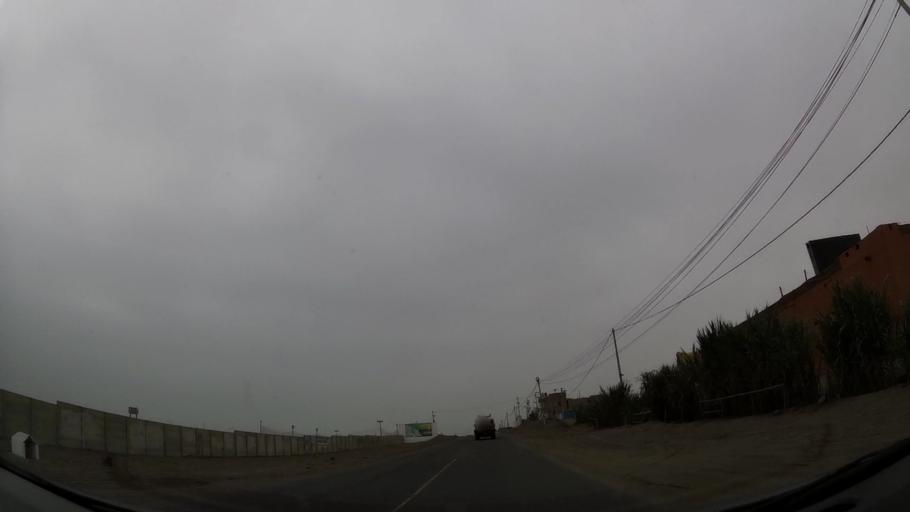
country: PE
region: Lima
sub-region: Lima
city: Punta Hermosa
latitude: -12.3258
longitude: -76.8260
